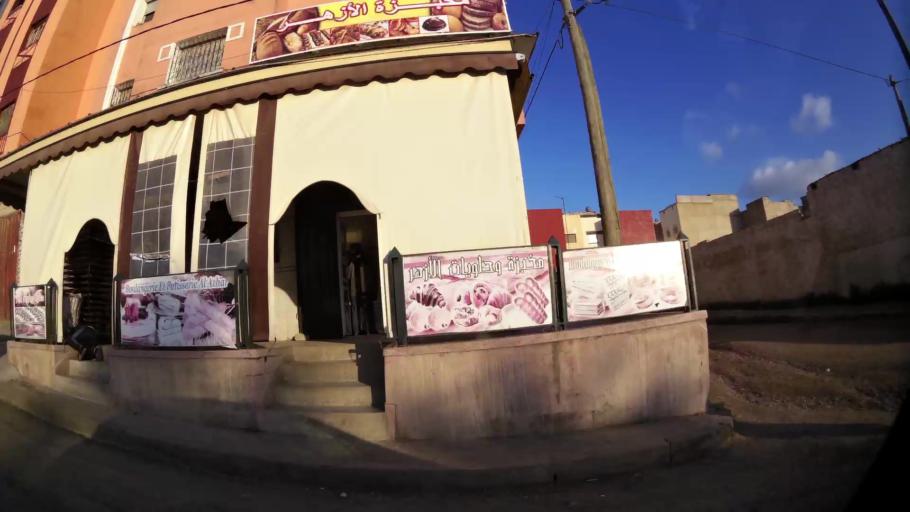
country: MA
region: Chaouia-Ouardigha
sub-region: Settat Province
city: Settat
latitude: 32.9960
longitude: -7.6044
